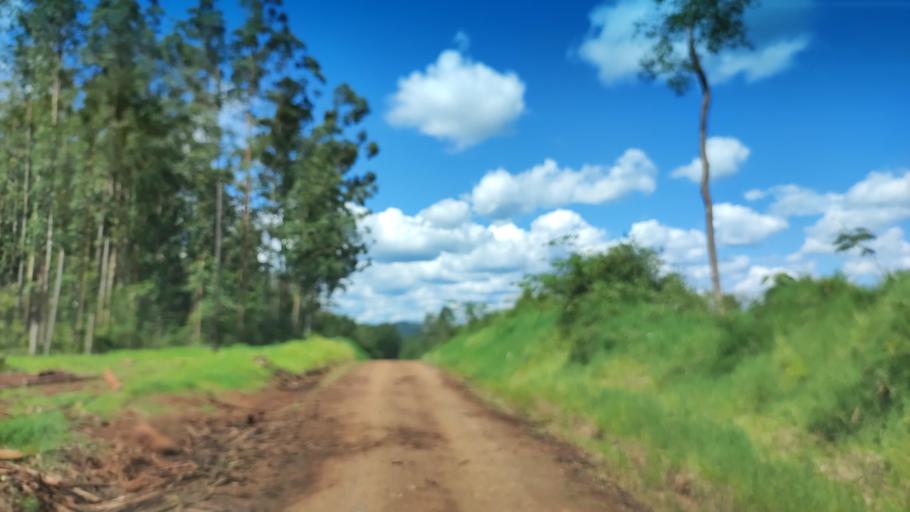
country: AR
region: Misiones
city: Ruiz de Montoya
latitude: -26.9528
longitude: -55.0197
